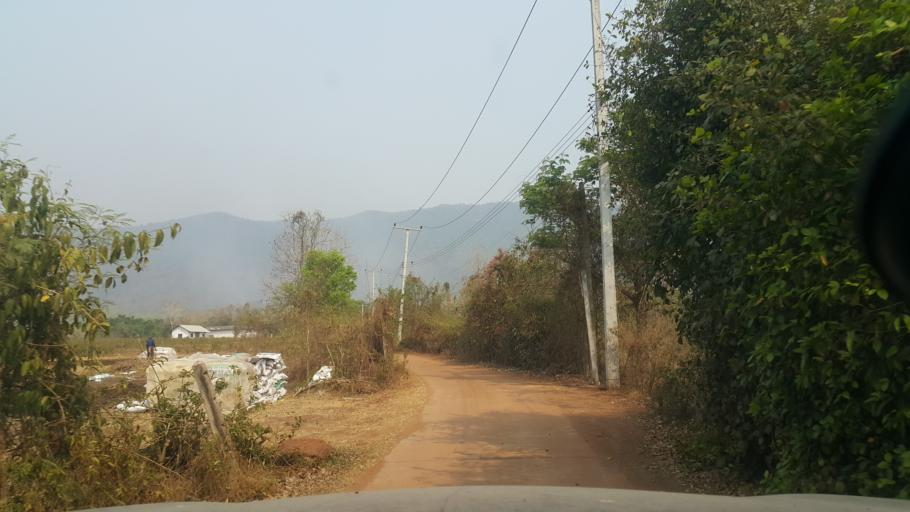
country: TH
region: Chiang Mai
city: Mae On
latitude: 18.7617
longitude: 99.2627
